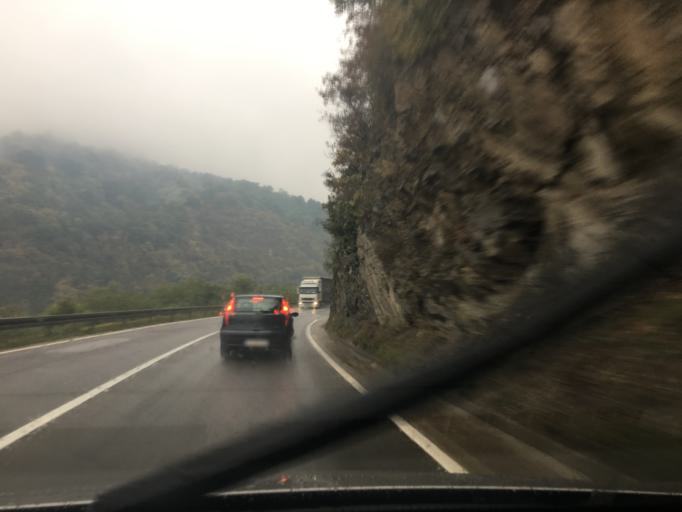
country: RS
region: Central Serbia
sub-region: Pcinjski Okrug
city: Vladicin Han
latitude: 42.7347
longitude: 22.0602
